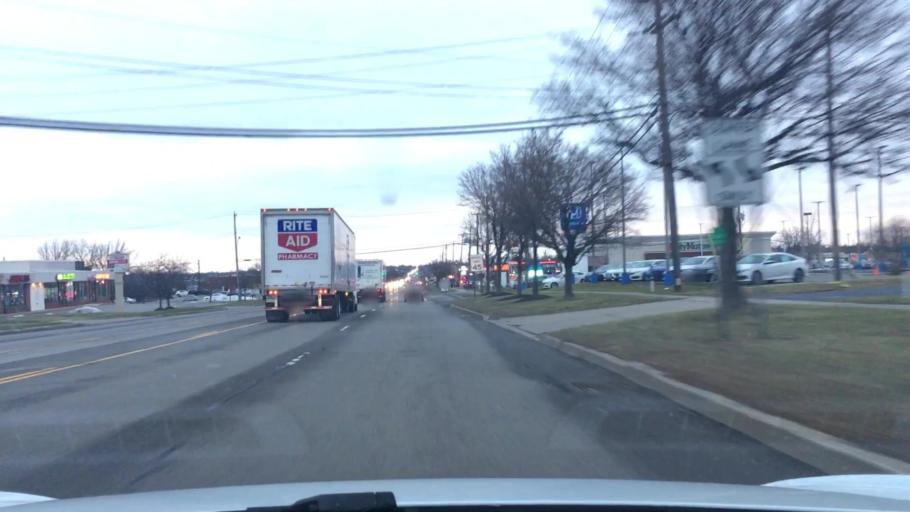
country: US
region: New York
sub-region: Erie County
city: Harris Hill
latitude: 42.9803
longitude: -78.6969
